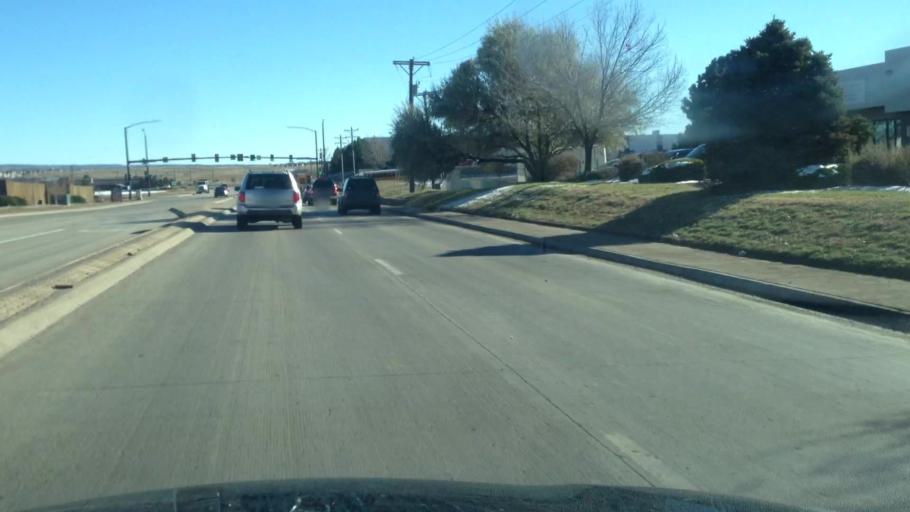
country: US
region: Colorado
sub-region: Arapahoe County
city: Dove Valley
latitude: 39.5878
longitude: -104.8170
